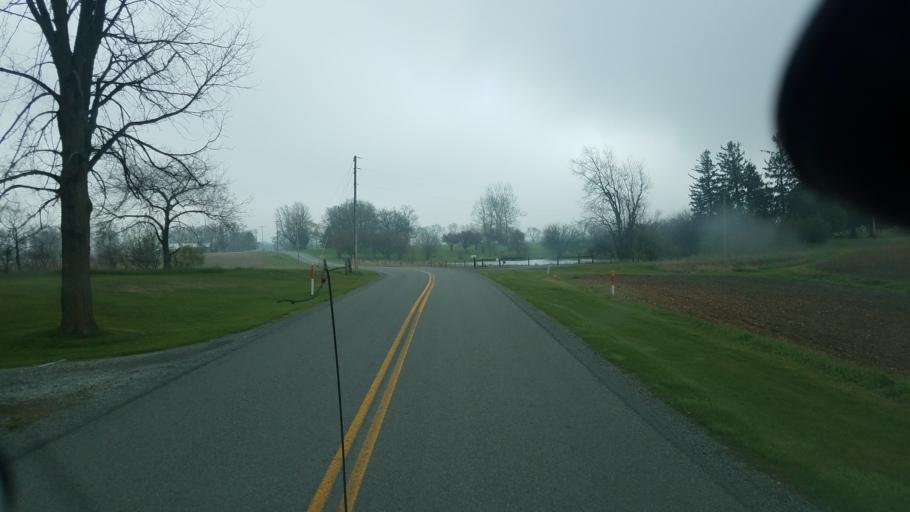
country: US
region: Ohio
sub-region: Logan County
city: Bellefontaine
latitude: 40.4021
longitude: -83.8095
